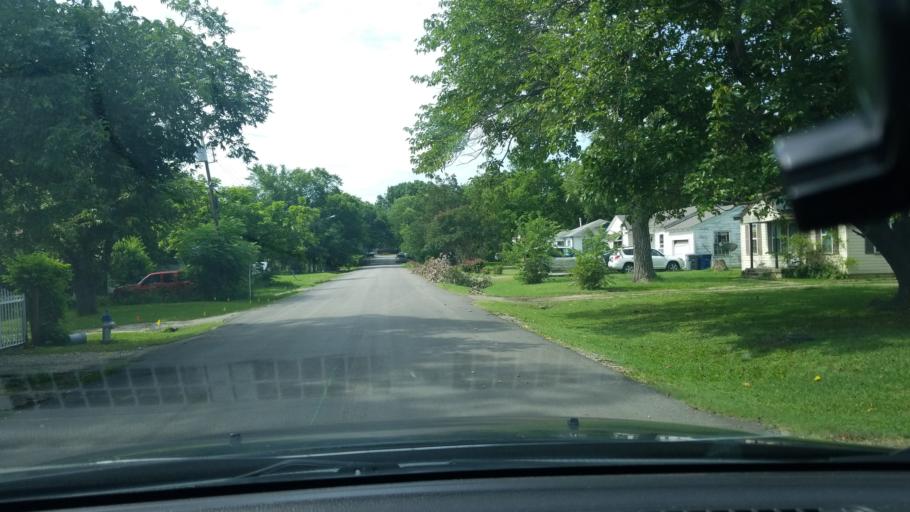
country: US
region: Texas
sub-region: Dallas County
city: Balch Springs
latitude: 32.7659
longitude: -96.6749
